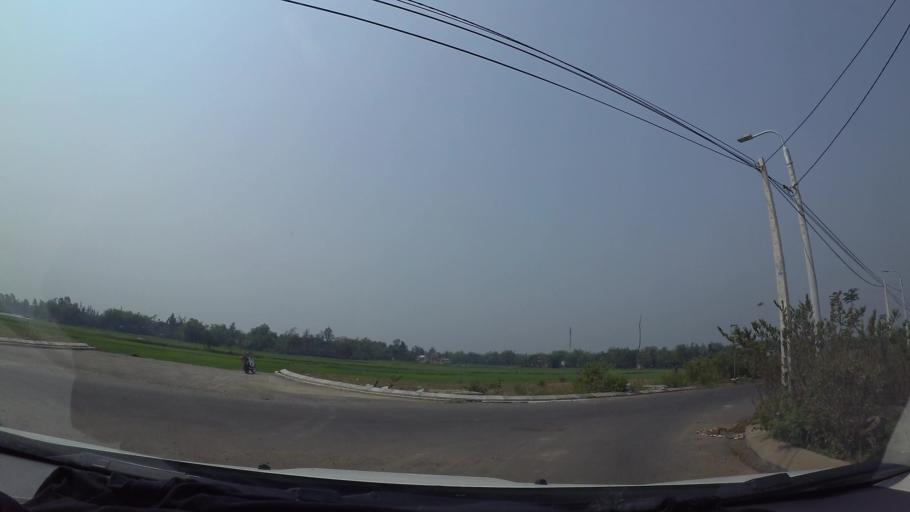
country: VN
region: Da Nang
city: Cam Le
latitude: 15.9812
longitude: 108.2272
